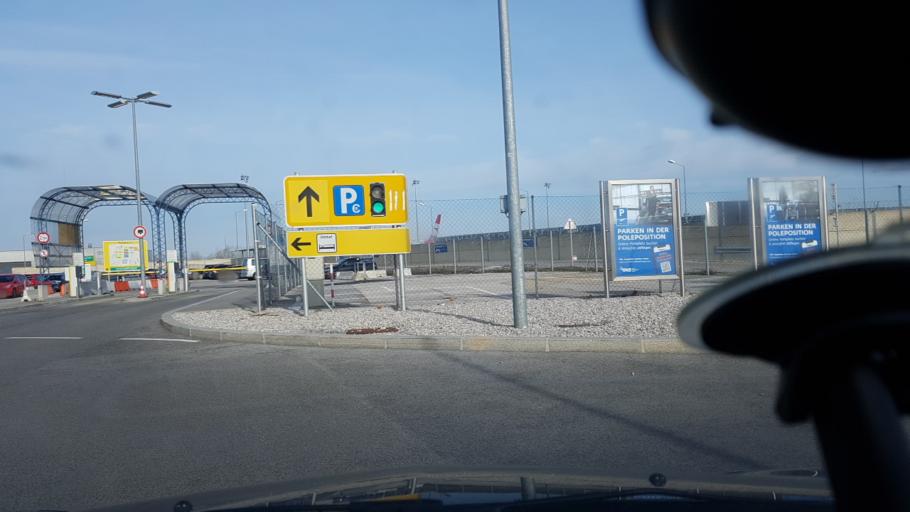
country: AT
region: Lower Austria
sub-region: Politischer Bezirk Wien-Umgebung
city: Fischamend Dorf
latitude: 48.1230
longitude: 16.5666
